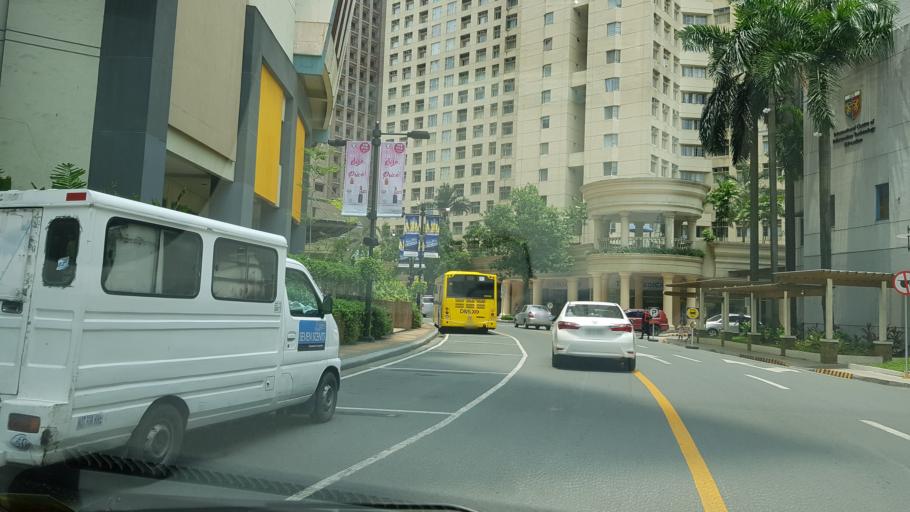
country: PH
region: Metro Manila
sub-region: Marikina
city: Calumpang
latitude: 14.6109
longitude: 121.0802
